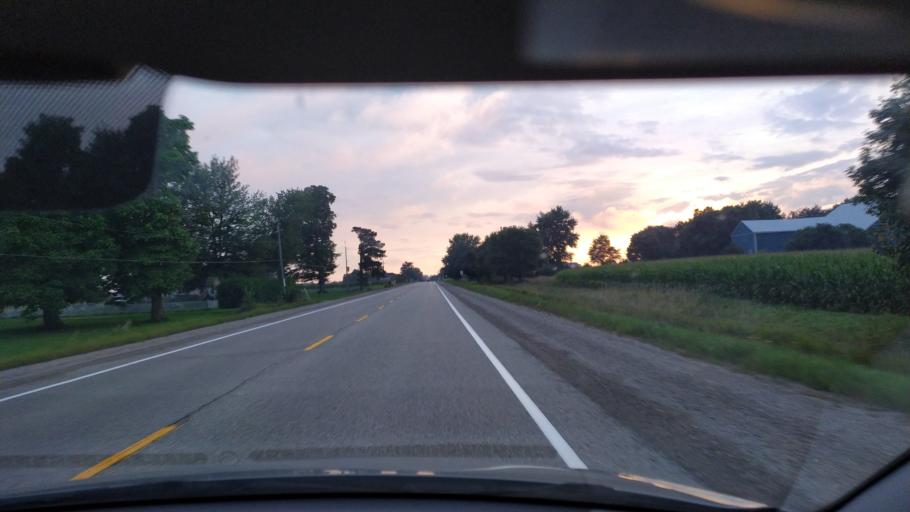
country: CA
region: Ontario
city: Kitchener
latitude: 43.3060
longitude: -80.6042
